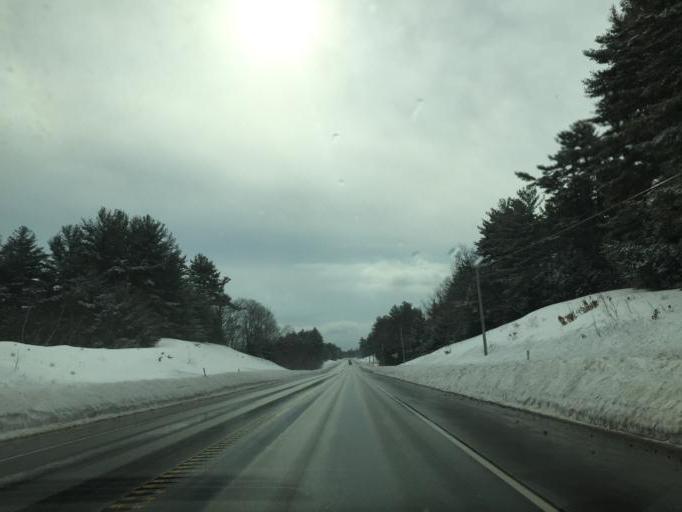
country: US
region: New Hampshire
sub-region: Carroll County
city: Sanbornville
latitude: 43.5399
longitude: -71.0324
